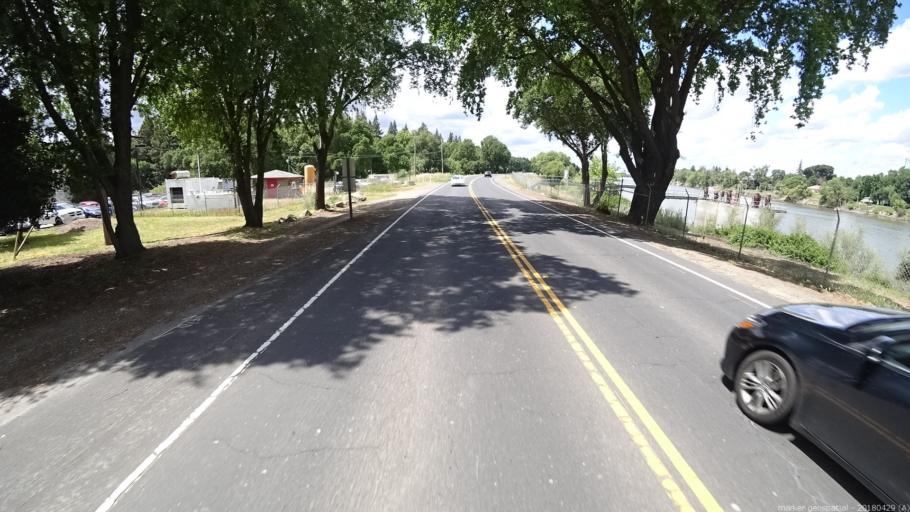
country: US
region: California
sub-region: Yolo County
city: West Sacramento
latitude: 38.5973
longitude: -121.5492
